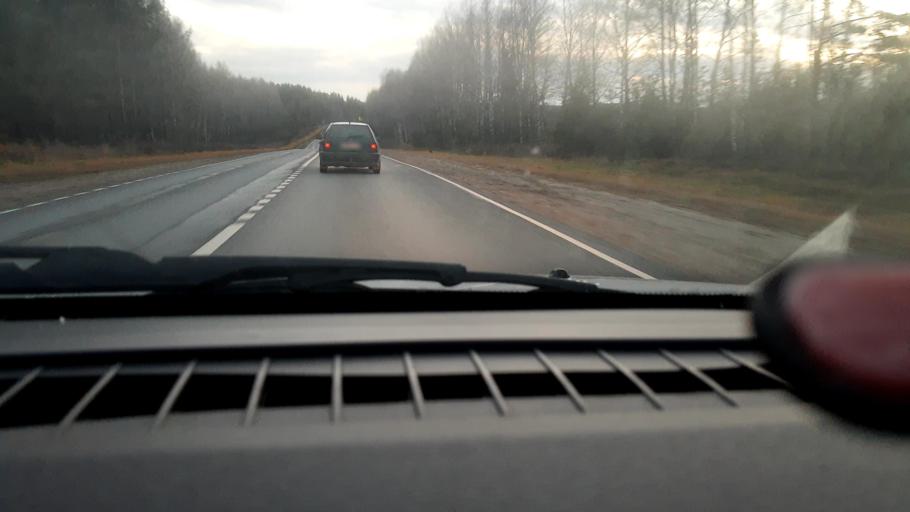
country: RU
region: Nizjnij Novgorod
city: Krasnyye Baki
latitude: 57.0365
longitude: 45.1242
